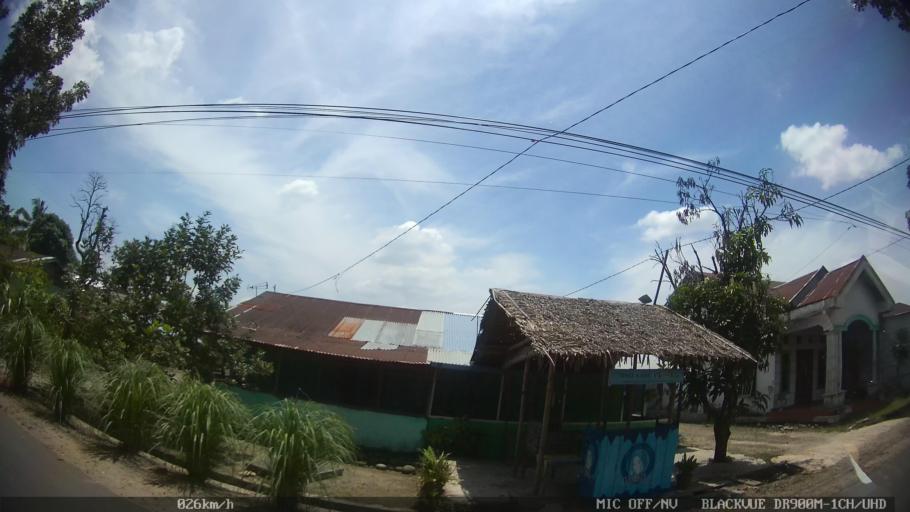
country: ID
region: North Sumatra
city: Binjai
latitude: 3.5940
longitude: 98.5182
